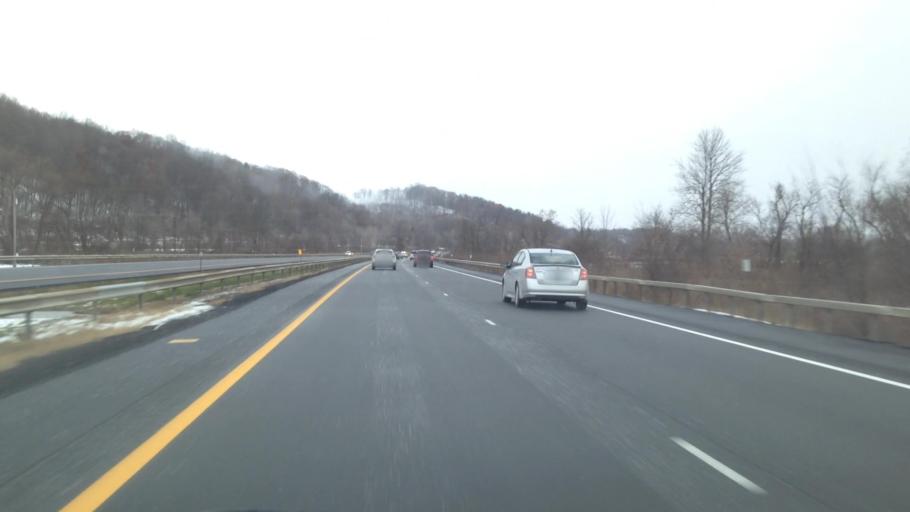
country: US
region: New York
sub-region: Montgomery County
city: Canajoharie
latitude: 42.9112
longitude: -74.5980
